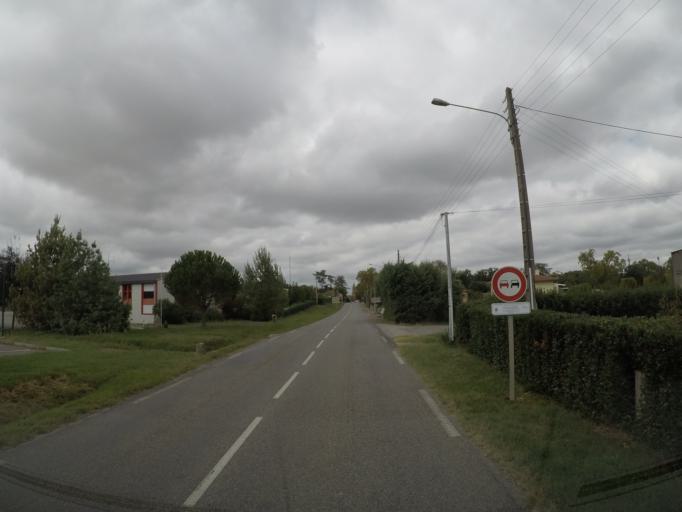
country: FR
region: Midi-Pyrenees
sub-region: Departement de l'Ariege
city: Lezat-sur-Leze
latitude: 43.2690
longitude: 1.3505
